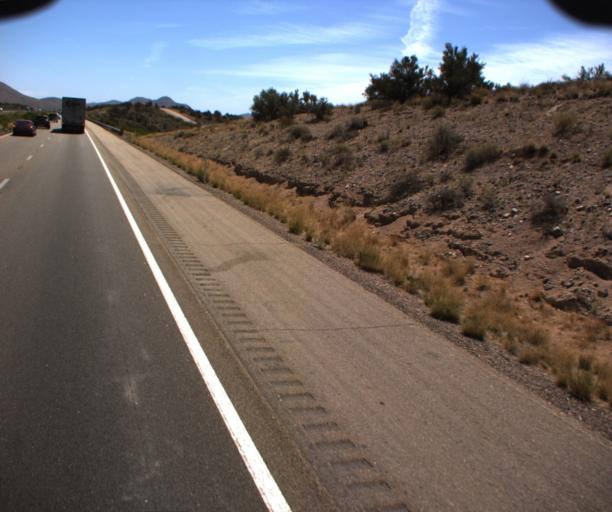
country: US
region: Arizona
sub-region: Mohave County
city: Peach Springs
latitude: 35.1603
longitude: -113.6081
